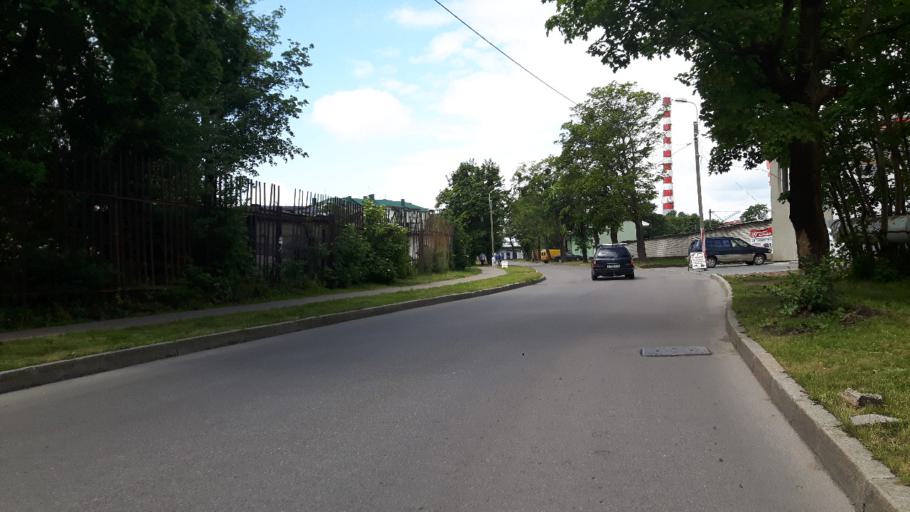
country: RU
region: Kaliningrad
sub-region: Gorod Kaliningrad
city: Kaliningrad
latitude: 54.7348
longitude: 20.5153
